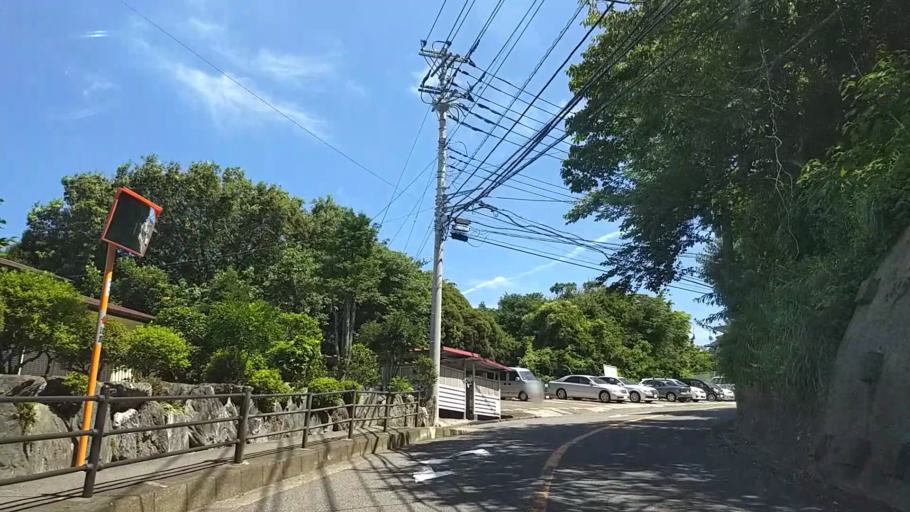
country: JP
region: Kanagawa
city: Zushi
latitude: 35.2923
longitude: 139.5908
